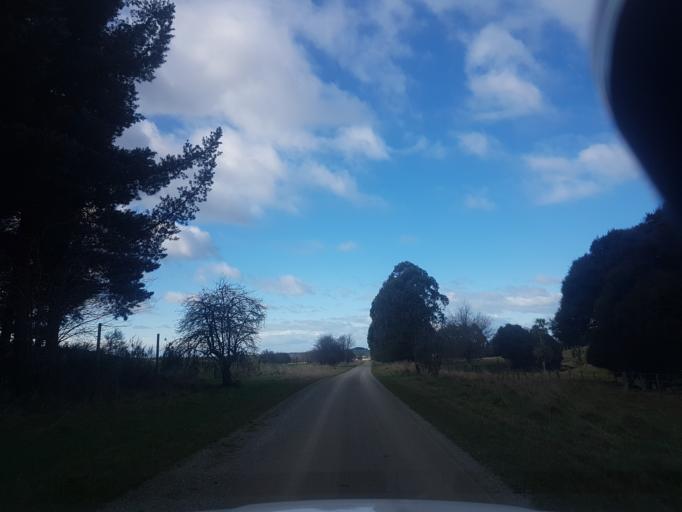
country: NZ
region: Canterbury
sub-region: Timaru District
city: Pleasant Point
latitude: -44.1881
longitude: 171.1678
